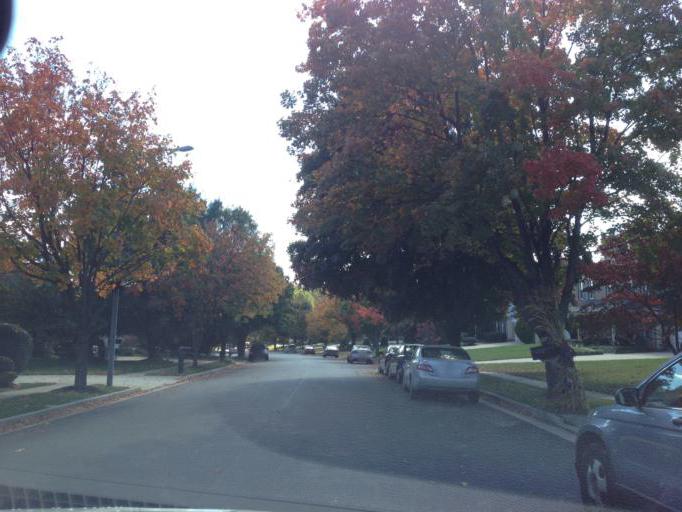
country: US
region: Maryland
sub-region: Howard County
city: North Laurel
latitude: 39.1407
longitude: -76.8953
